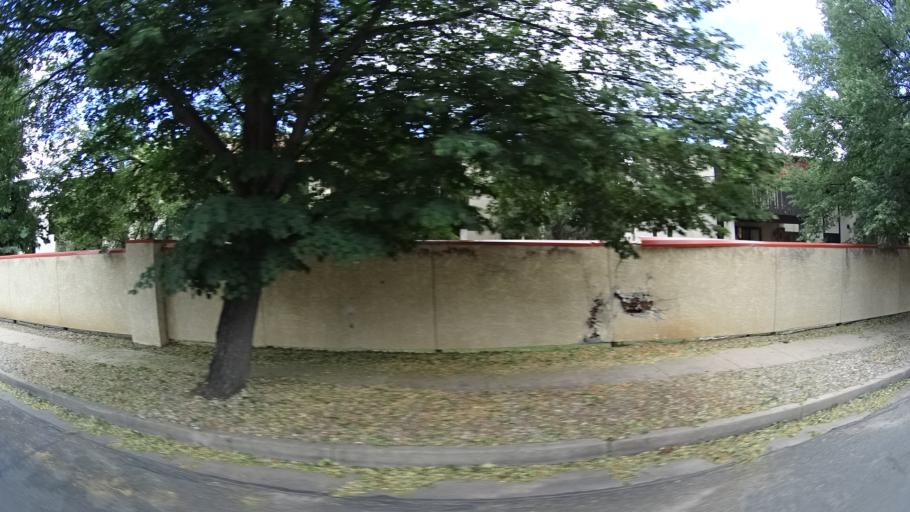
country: US
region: Colorado
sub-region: El Paso County
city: Stratmoor
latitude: 38.7869
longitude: -104.8241
